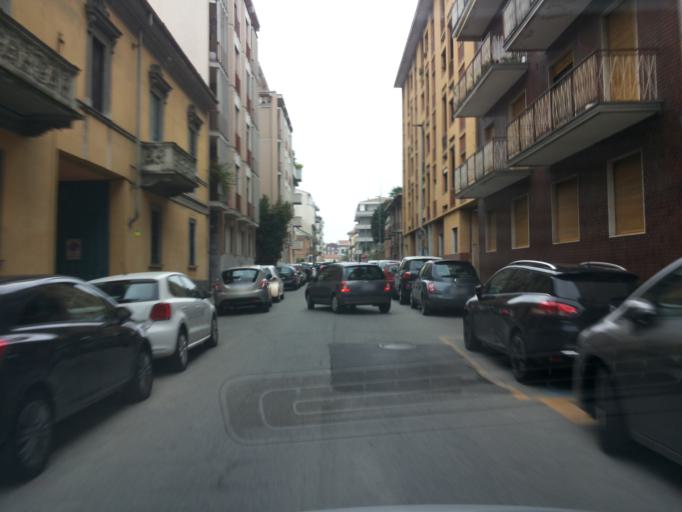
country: IT
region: Piedmont
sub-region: Provincia di Novara
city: Novara
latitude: 45.4413
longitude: 8.6086
